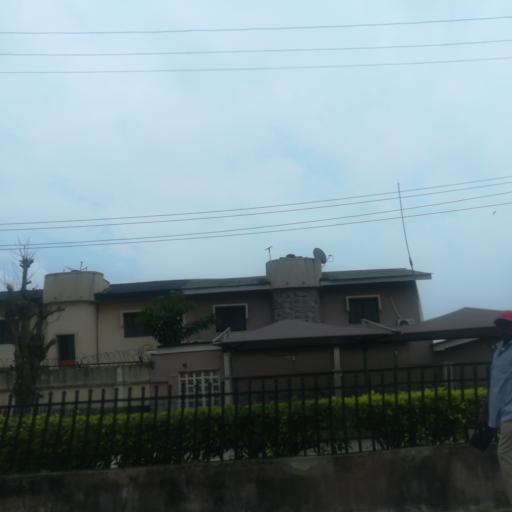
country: NG
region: Lagos
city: Ojota
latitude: 6.5806
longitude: 3.3839
